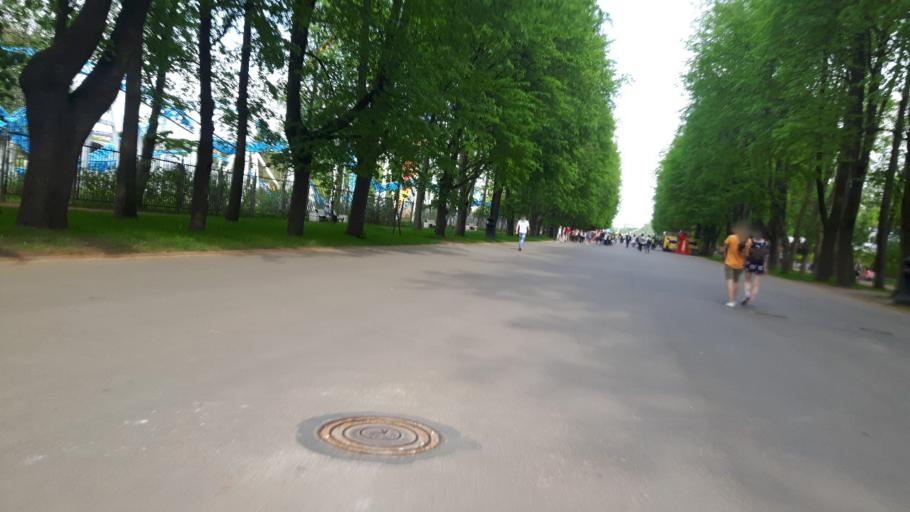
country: RU
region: Leningrad
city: Krestovskiy ostrov
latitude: 59.9715
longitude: 30.2517
